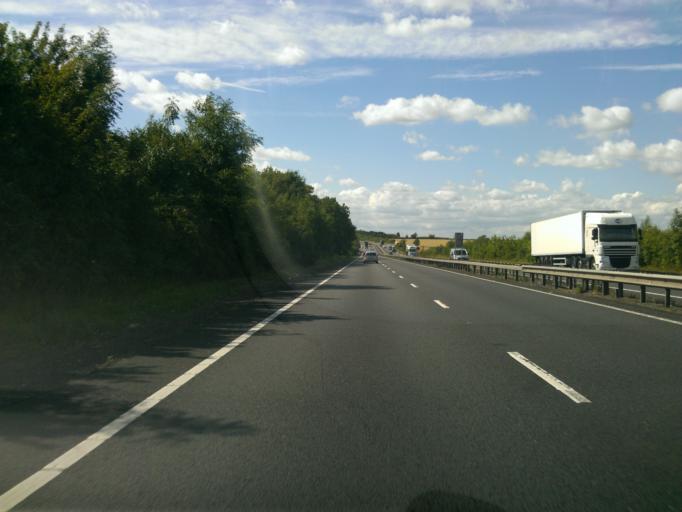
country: GB
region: England
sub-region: Northamptonshire
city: Thrapston
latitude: 52.3765
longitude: -0.4688
